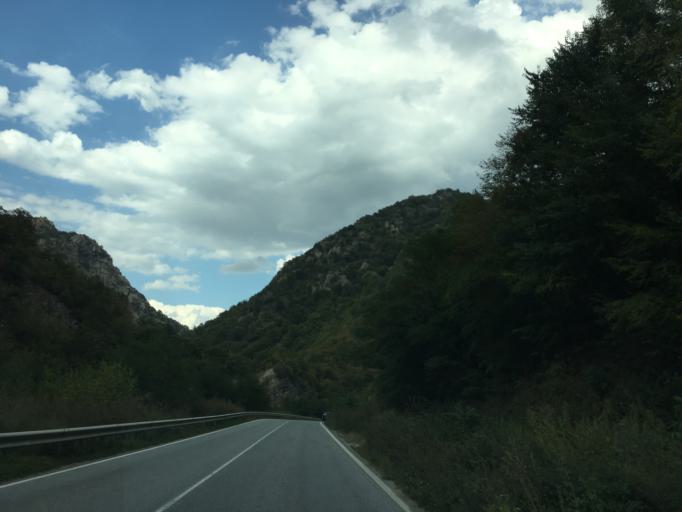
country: BG
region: Pazardzhik
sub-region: Obshtina Septemvri
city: Septemvri
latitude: 42.1046
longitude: 24.1037
